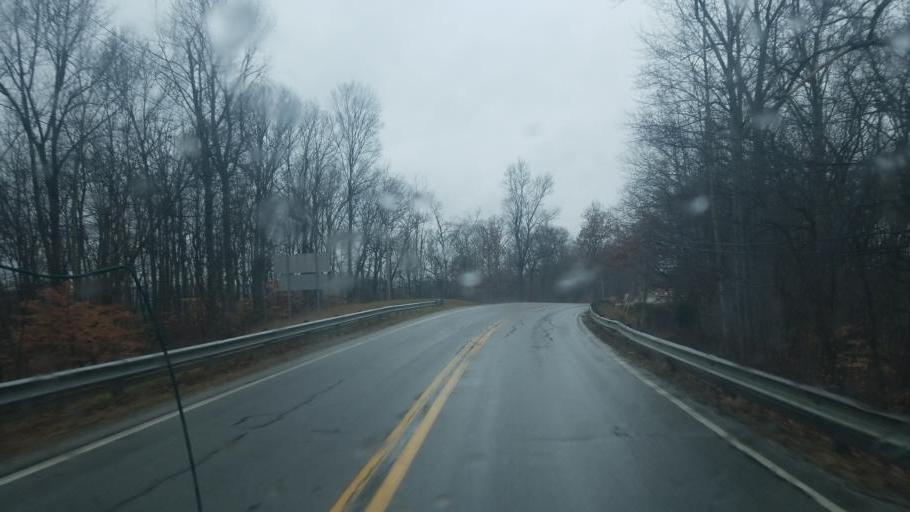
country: US
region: Indiana
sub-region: Brown County
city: Nashville
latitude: 39.1750
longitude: -86.2716
